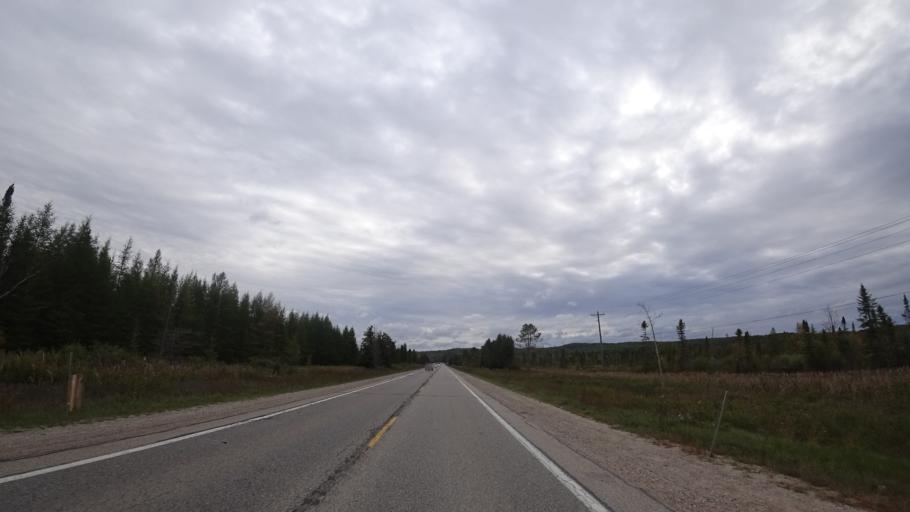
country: US
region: Michigan
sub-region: Charlevoix County
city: Boyne City
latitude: 45.2257
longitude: -84.9200
